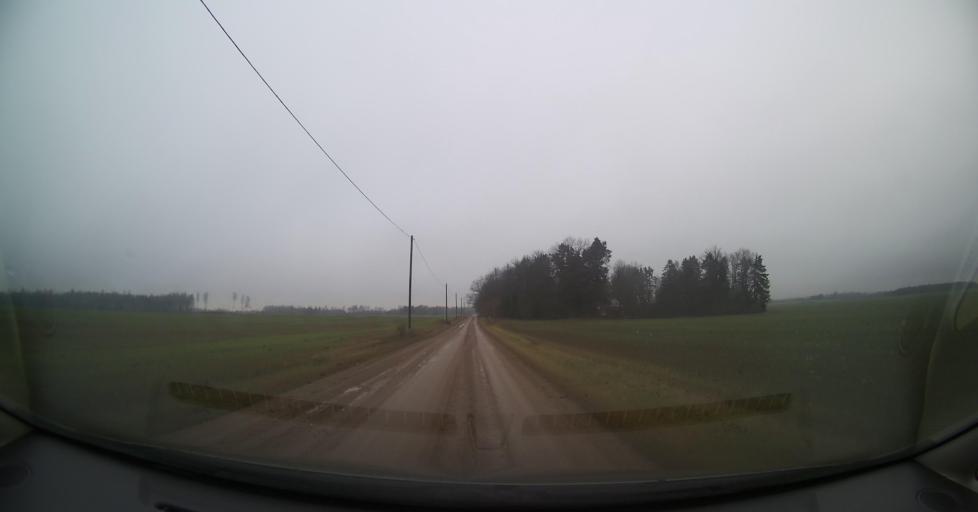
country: EE
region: Tartu
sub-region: Tartu linn
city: Tartu
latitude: 58.3817
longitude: 26.9266
